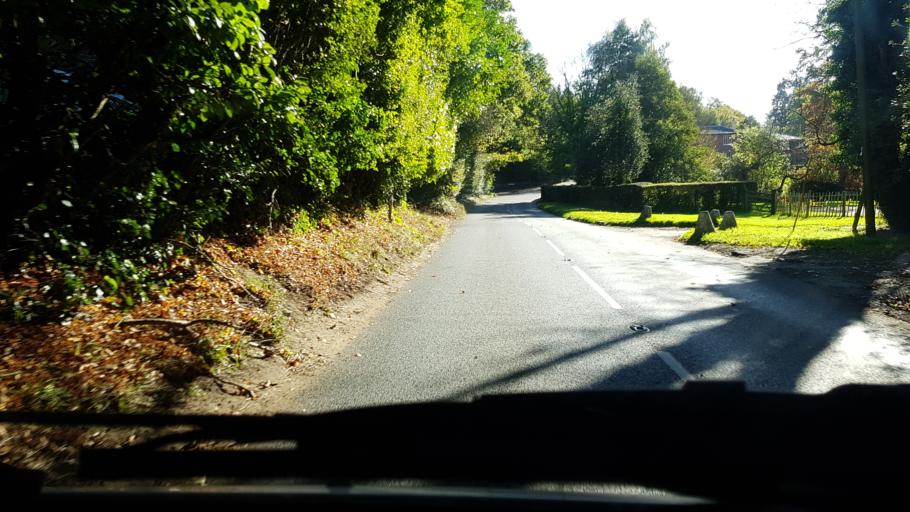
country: GB
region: England
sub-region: Surrey
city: Chilworth
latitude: 51.1947
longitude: -0.5348
